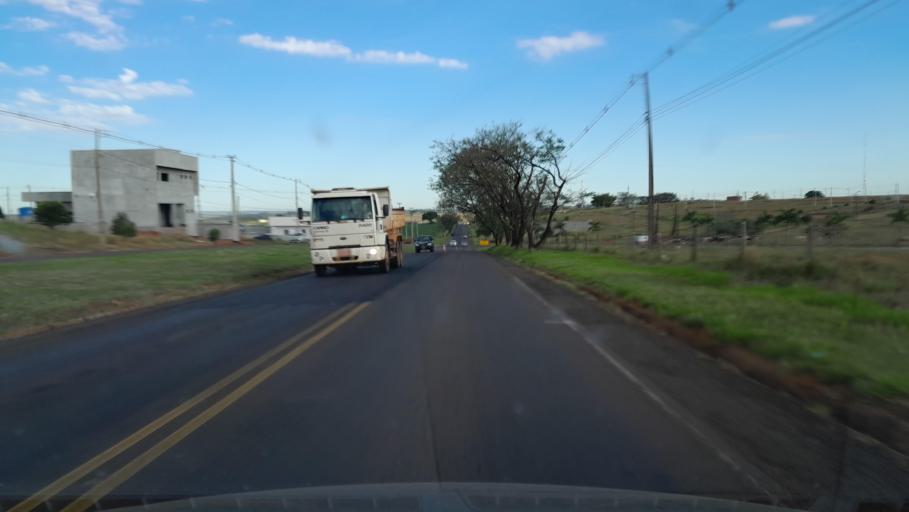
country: BR
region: Parana
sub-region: Umuarama
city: Umuarama
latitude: -23.7620
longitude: -53.2707
